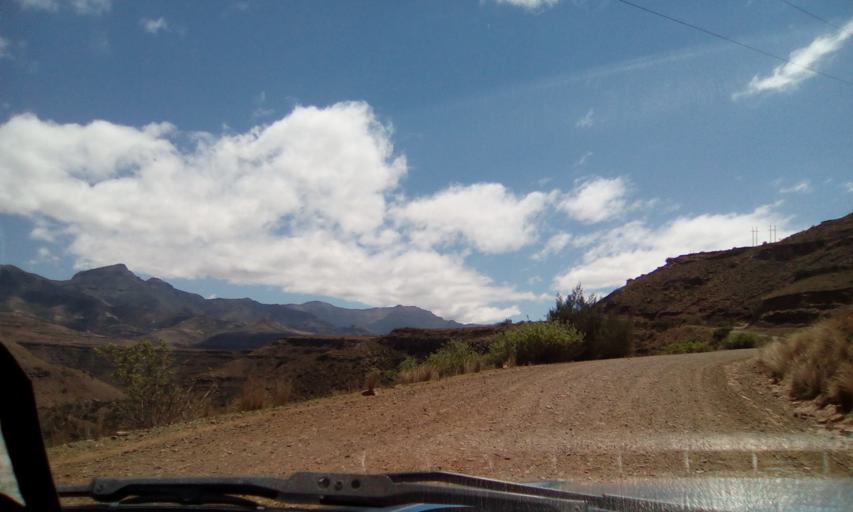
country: LS
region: Qacha's Nek
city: Qacha's Nek
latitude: -30.0682
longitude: 28.6233
